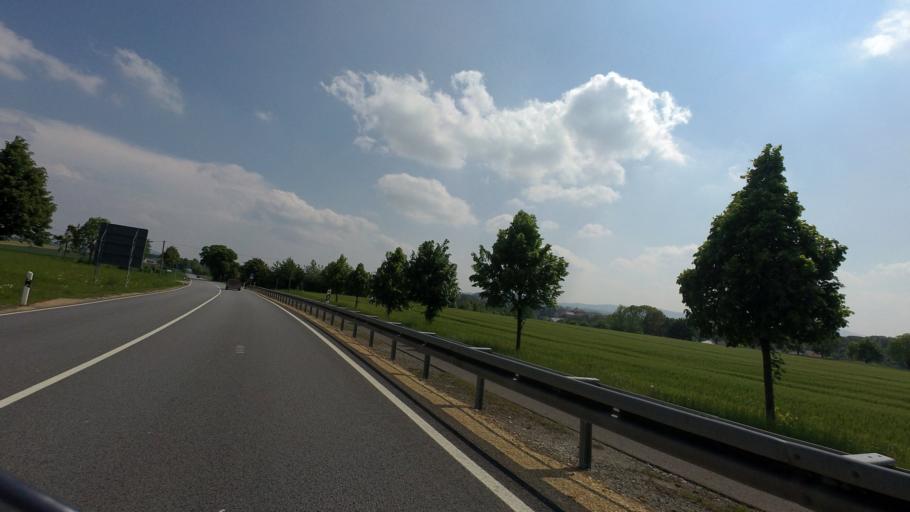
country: DE
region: Saxony
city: Weissenberg
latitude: 51.2037
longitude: 14.6643
